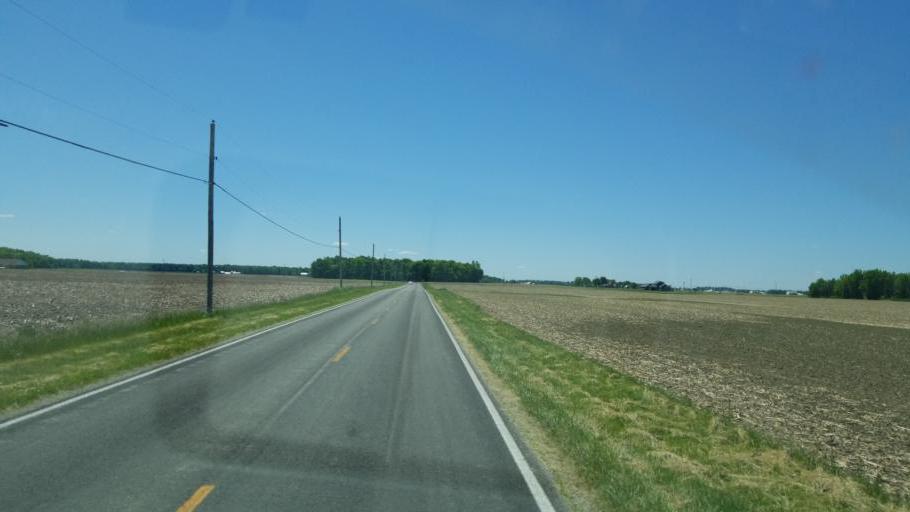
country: US
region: Ohio
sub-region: Shelby County
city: Fort Loramie
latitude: 40.3589
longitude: -84.3386
